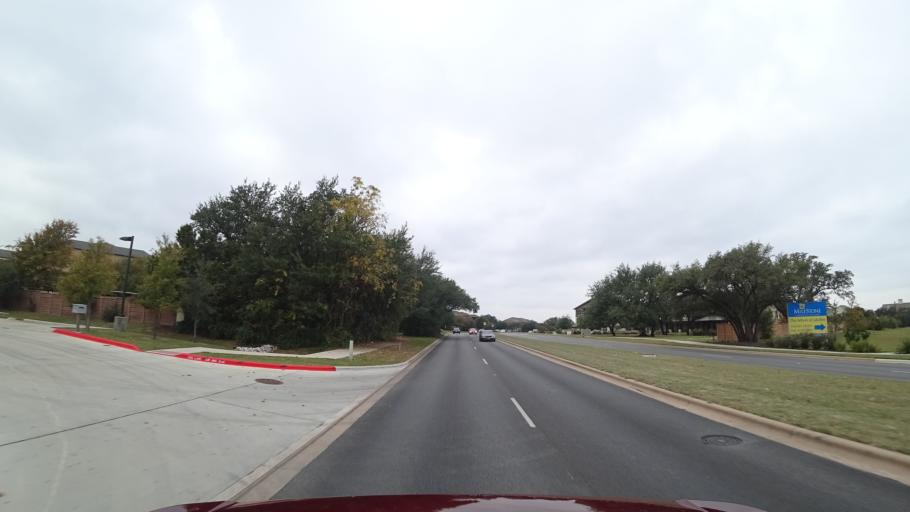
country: US
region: Texas
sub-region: Williamson County
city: Cedar Park
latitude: 30.4791
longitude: -97.8209
